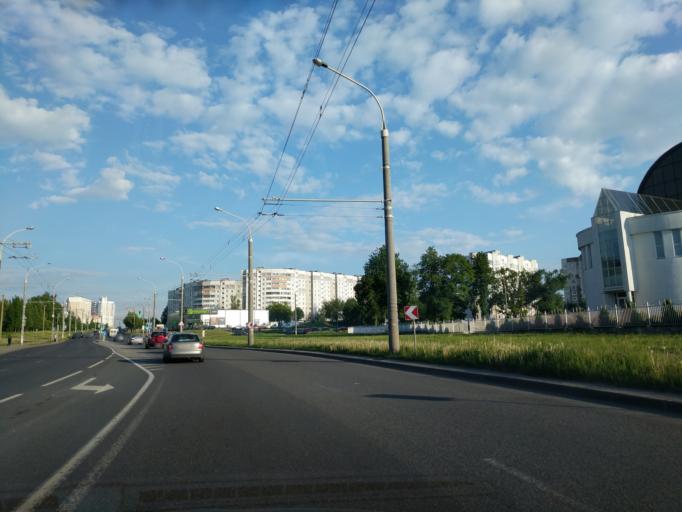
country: BY
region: Minsk
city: Novoye Medvezhino
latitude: 53.8929
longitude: 27.4358
